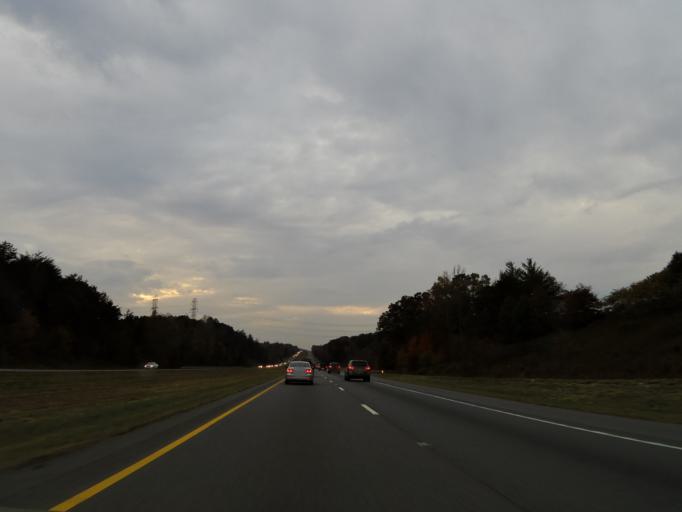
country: US
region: North Carolina
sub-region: Catawba County
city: Longview
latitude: 35.7062
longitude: -81.3962
